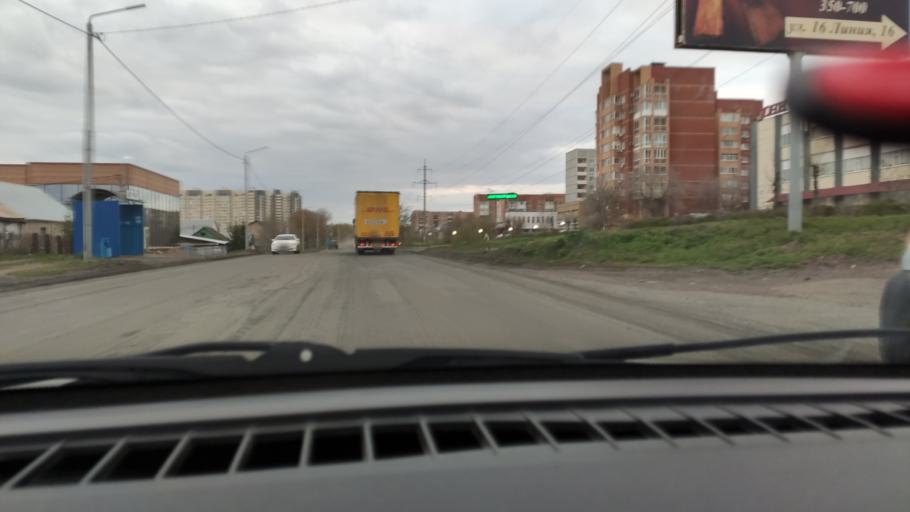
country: RU
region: Orenburg
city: Orenburg
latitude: 51.7858
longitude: 55.1805
